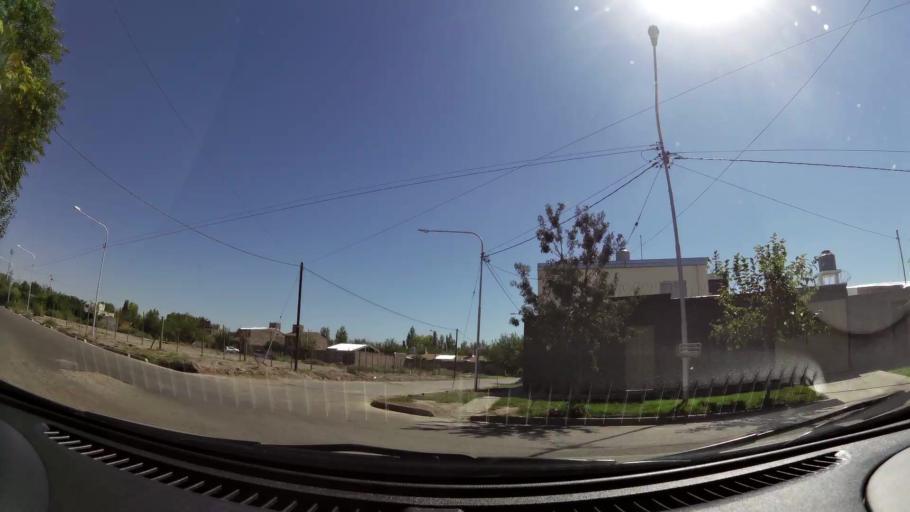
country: AR
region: Mendoza
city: Villa Nueva
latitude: -32.9008
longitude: -68.7764
